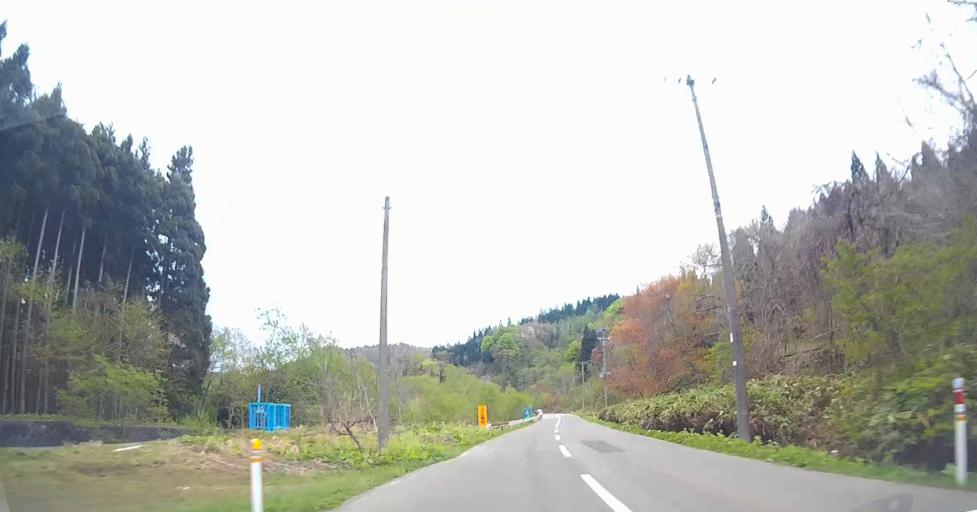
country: JP
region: Aomori
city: Goshogawara
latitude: 41.1203
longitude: 140.5234
